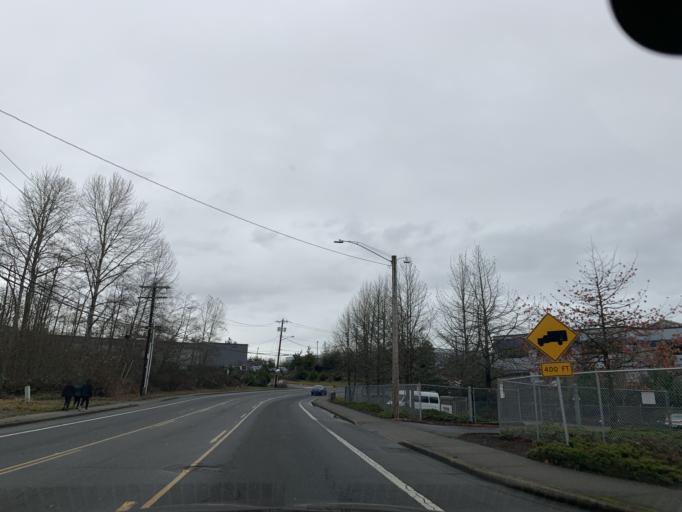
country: US
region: Washington
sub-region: Snohomish County
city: Mukilteo
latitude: 47.9210
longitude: -122.2630
